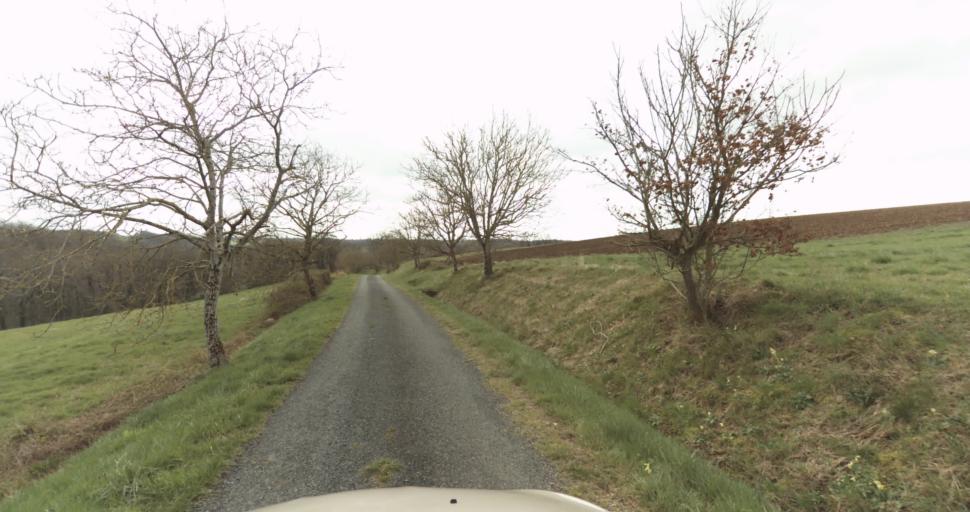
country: FR
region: Midi-Pyrenees
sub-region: Departement du Tarn
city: Frejairolles
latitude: 43.8528
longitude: 2.2231
